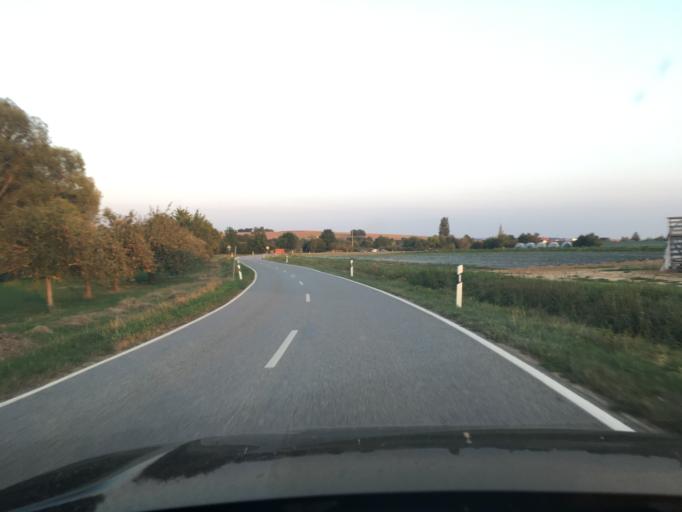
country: DE
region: Baden-Wuerttemberg
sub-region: Regierungsbezirk Stuttgart
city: Brackenheim
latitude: 49.0941
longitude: 9.0721
